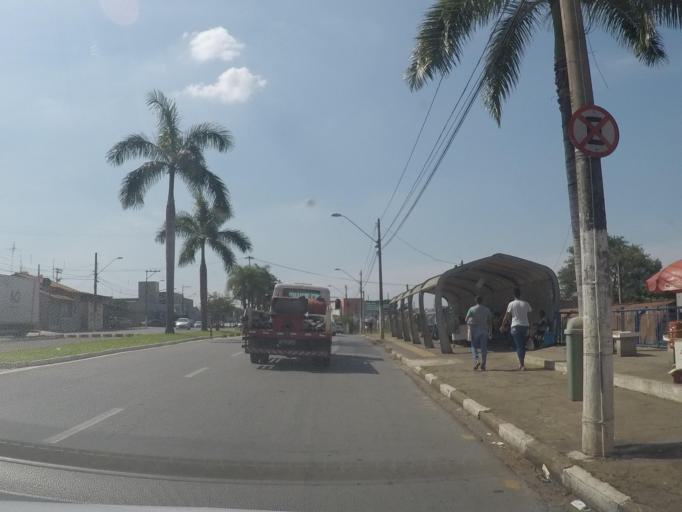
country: BR
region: Sao Paulo
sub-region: Sumare
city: Sumare
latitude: -22.8205
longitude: -47.2650
